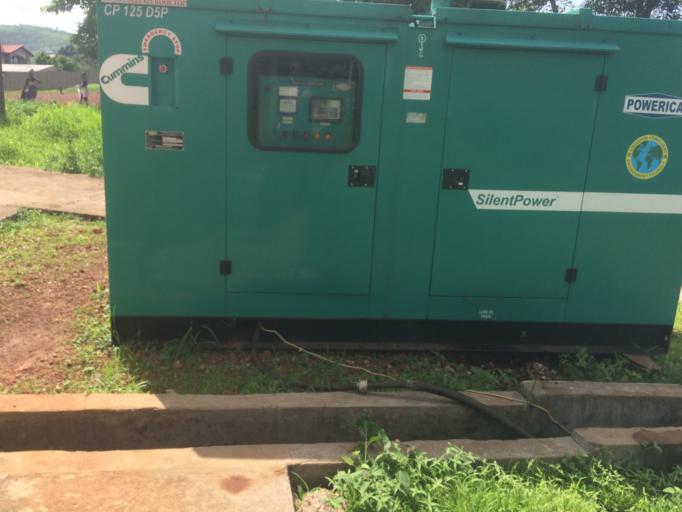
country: SL
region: Western Area
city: Hastings
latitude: 8.4107
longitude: -13.1566
